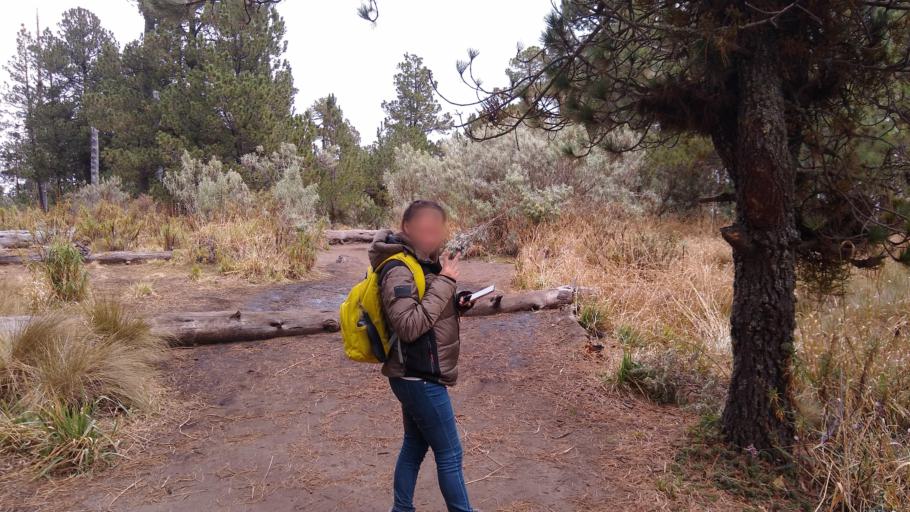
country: MX
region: Tlaxcala
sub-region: San Jose Teacalco
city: San Jose Teacalco
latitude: 19.2508
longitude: -98.0334
